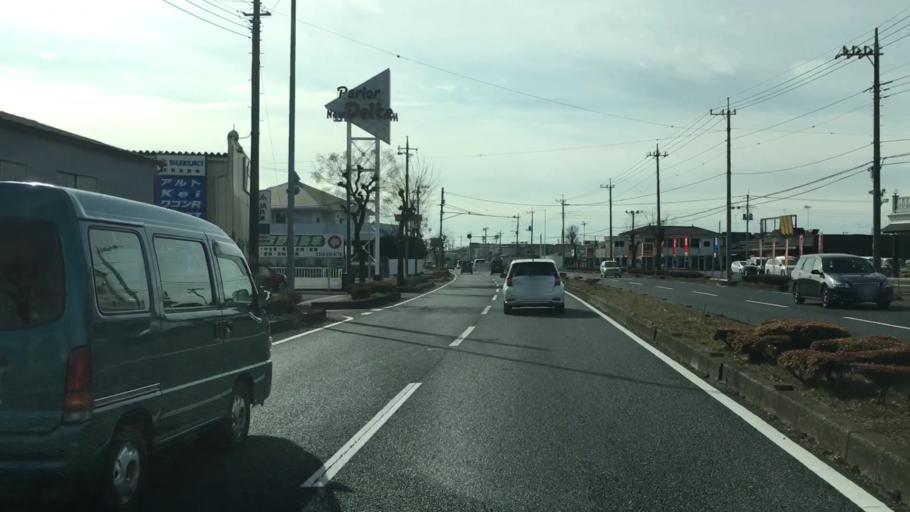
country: JP
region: Saitama
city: Menuma
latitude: 36.2307
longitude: 139.3715
